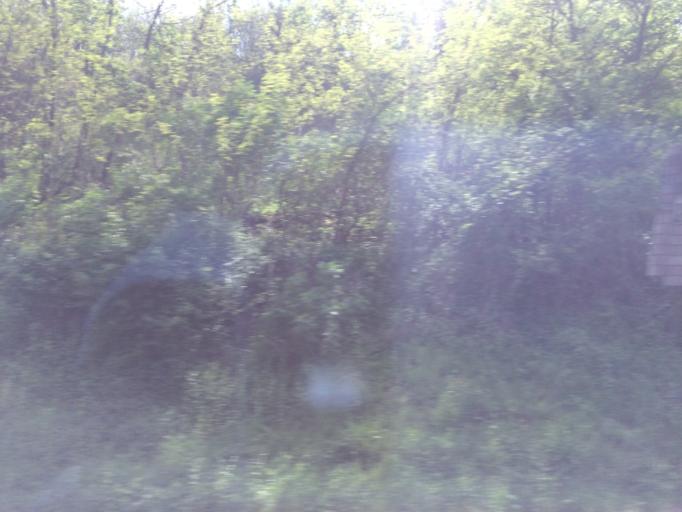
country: DE
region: Bavaria
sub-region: Regierungsbezirk Unterfranken
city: Gerbrunn
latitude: 49.7921
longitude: 9.9910
